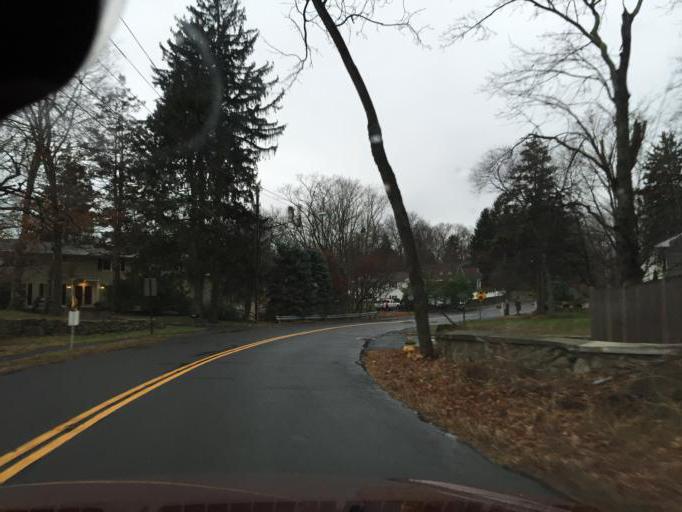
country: US
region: Connecticut
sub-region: Fairfield County
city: East Norwalk
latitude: 41.1238
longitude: -73.3799
